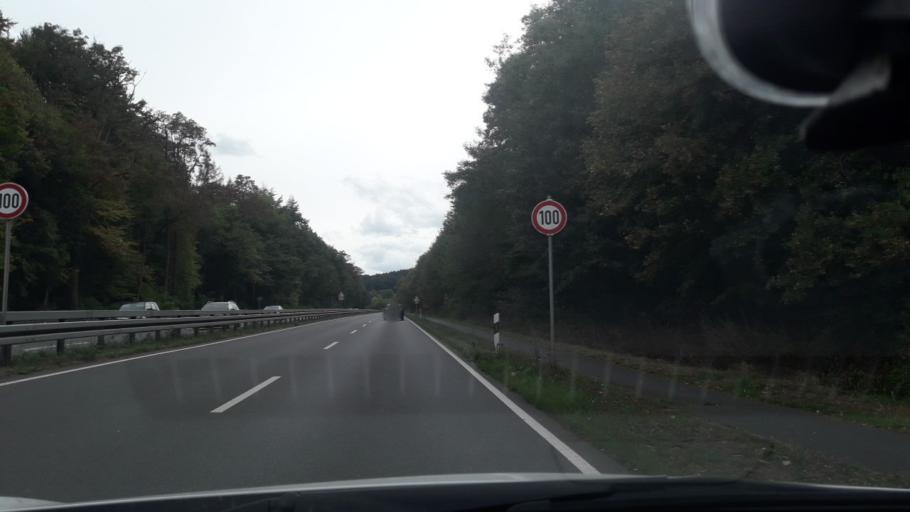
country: DE
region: Lower Saxony
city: Cramme
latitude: 52.0985
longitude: 10.3665
